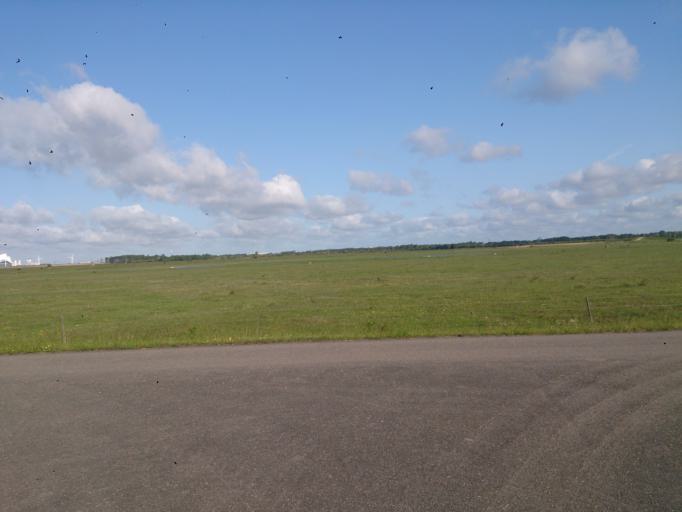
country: DK
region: Capital Region
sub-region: Tarnby Kommune
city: Tarnby
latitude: 55.5979
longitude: 12.5491
